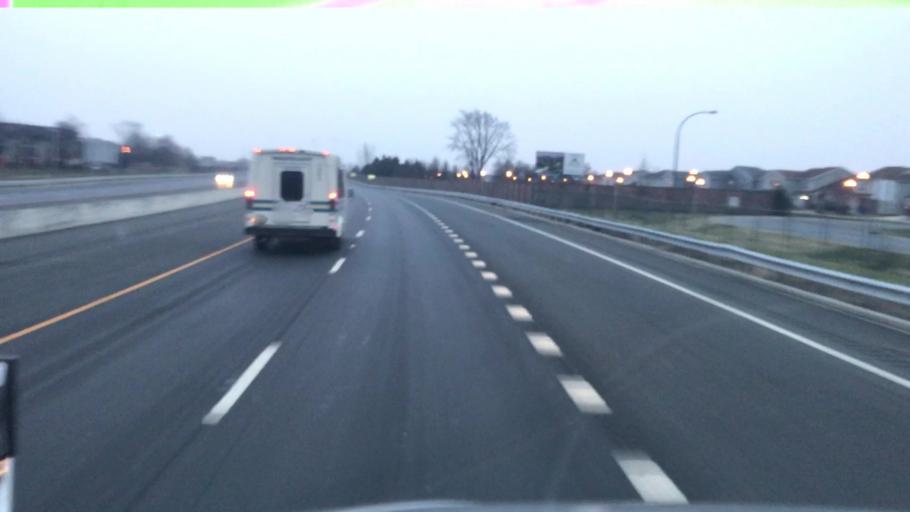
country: US
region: Delaware
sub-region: Kent County
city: Dover Base Housing
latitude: 39.1258
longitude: -75.4879
